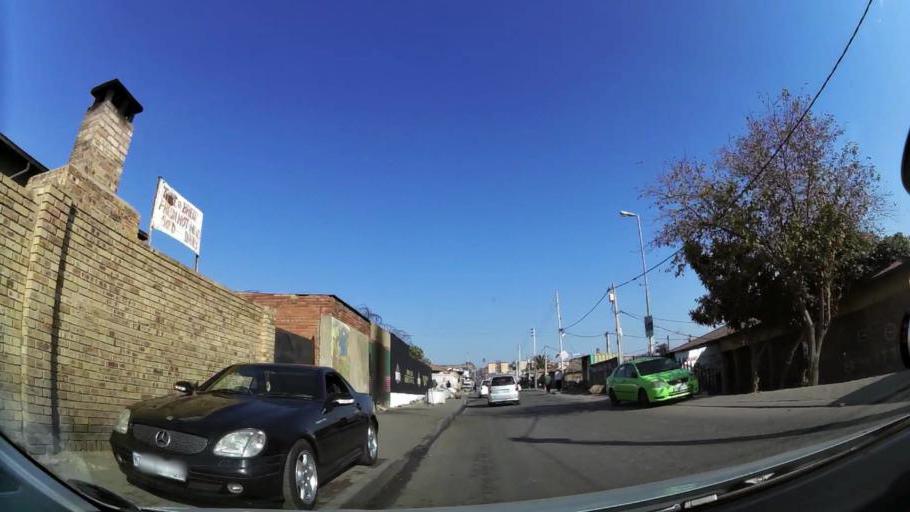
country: ZA
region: Gauteng
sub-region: City of Johannesburg Metropolitan Municipality
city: Modderfontein
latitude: -26.1068
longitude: 28.1039
